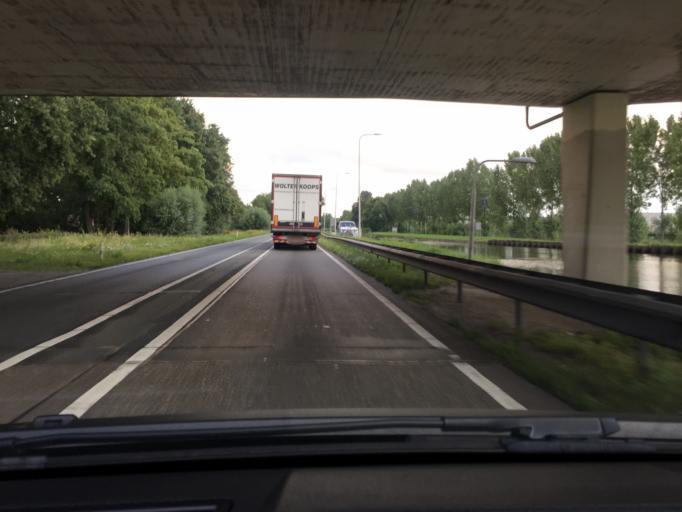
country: NL
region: North Brabant
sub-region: Gemeente Veghel
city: Veghel
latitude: 51.6084
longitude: 5.5325
